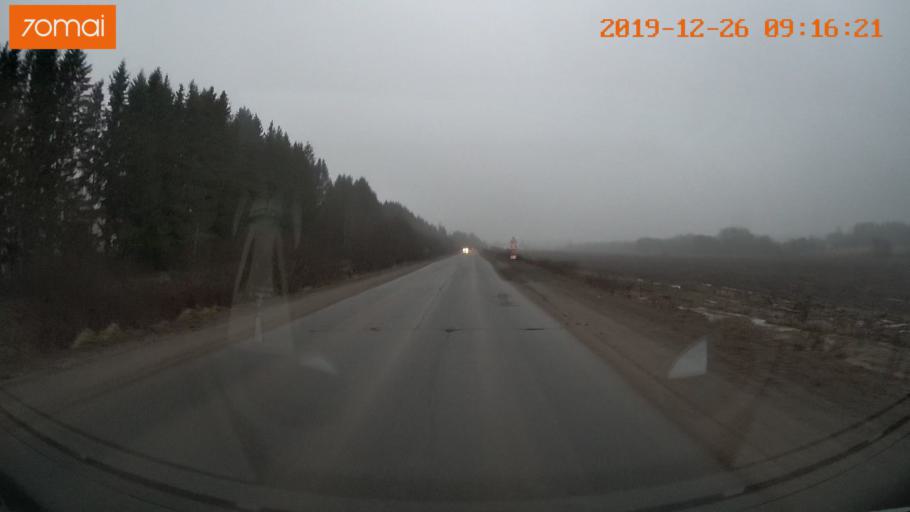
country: RU
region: Vologda
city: Gryazovets
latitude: 58.9170
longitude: 40.2389
